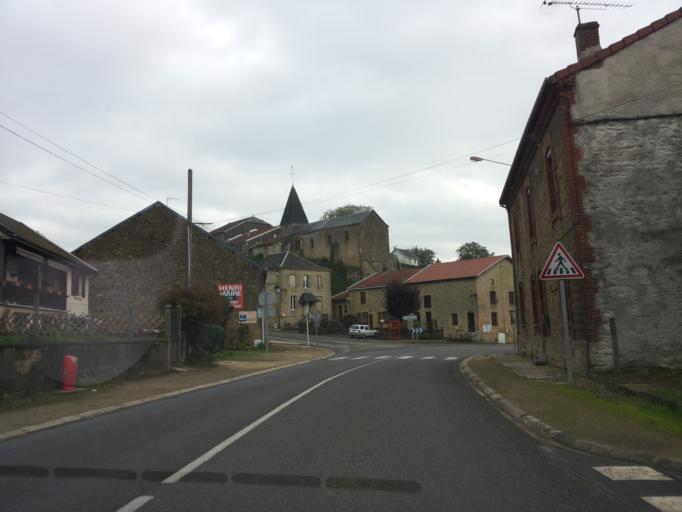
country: FR
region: Champagne-Ardenne
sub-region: Departement des Ardennes
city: Blagny
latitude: 49.6154
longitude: 5.2216
